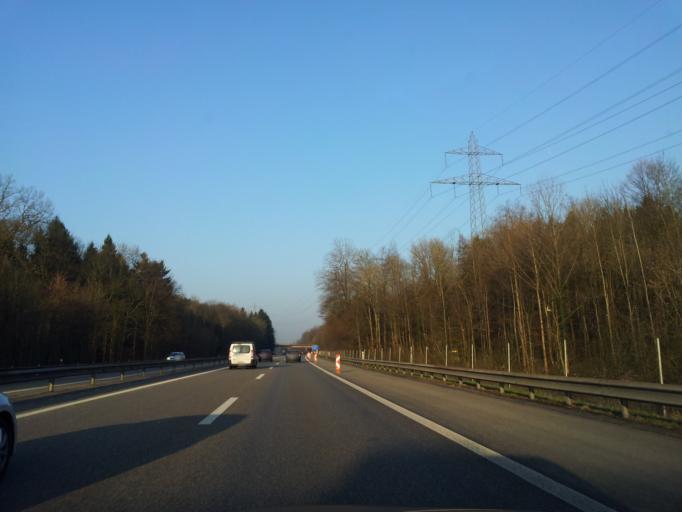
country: CH
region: Aargau
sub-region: Bezirk Rheinfelden
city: Magden
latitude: 47.5459
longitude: 7.8177
